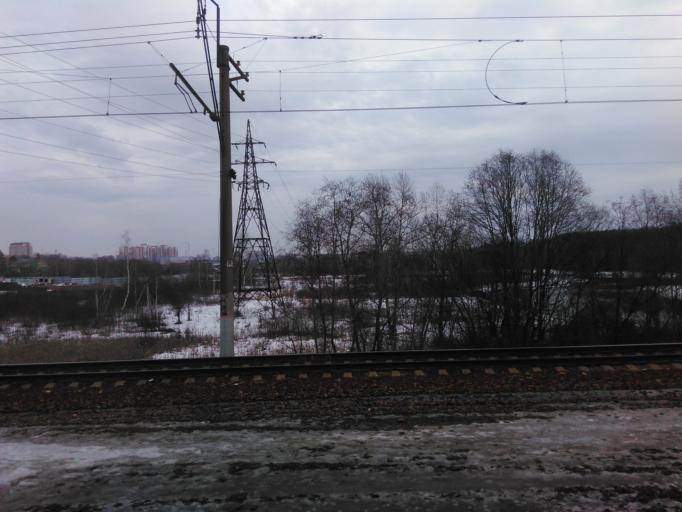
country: RU
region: Moskovskaya
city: Mamontovka
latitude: 55.9979
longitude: 37.8312
